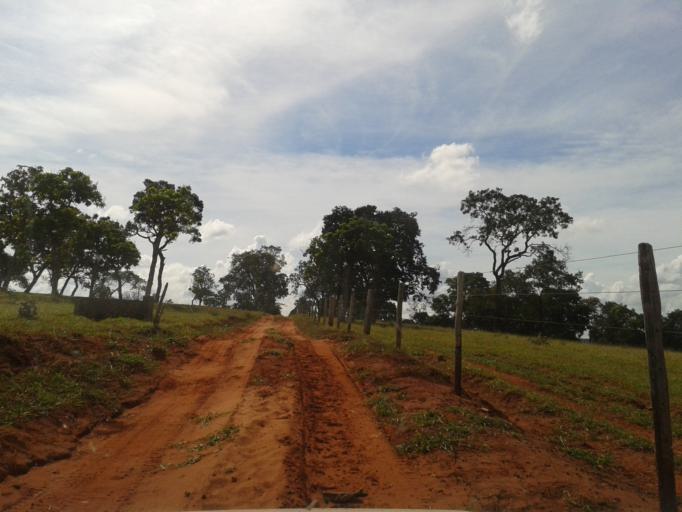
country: BR
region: Minas Gerais
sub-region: Campina Verde
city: Campina Verde
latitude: -19.4414
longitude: -49.6303
